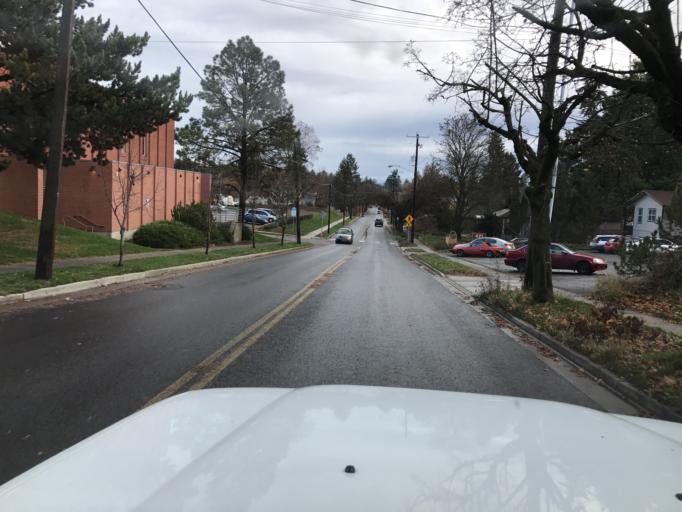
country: US
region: Idaho
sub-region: Latah County
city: Moscow
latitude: 46.7302
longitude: -116.9966
